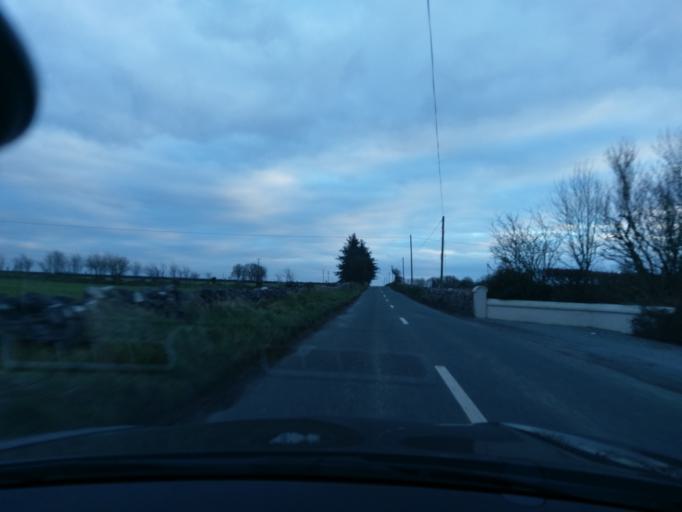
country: IE
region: Connaught
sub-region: County Galway
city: Athenry
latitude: 53.3763
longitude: -8.7741
